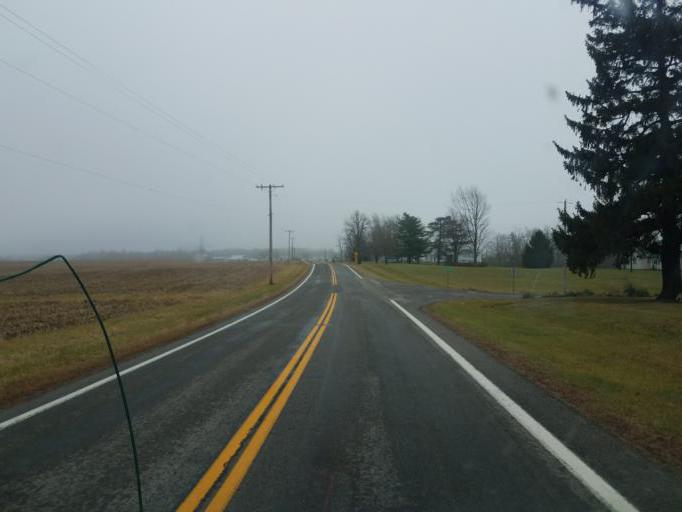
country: US
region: Ohio
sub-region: Champaign County
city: North Lewisburg
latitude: 40.2624
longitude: -83.5874
